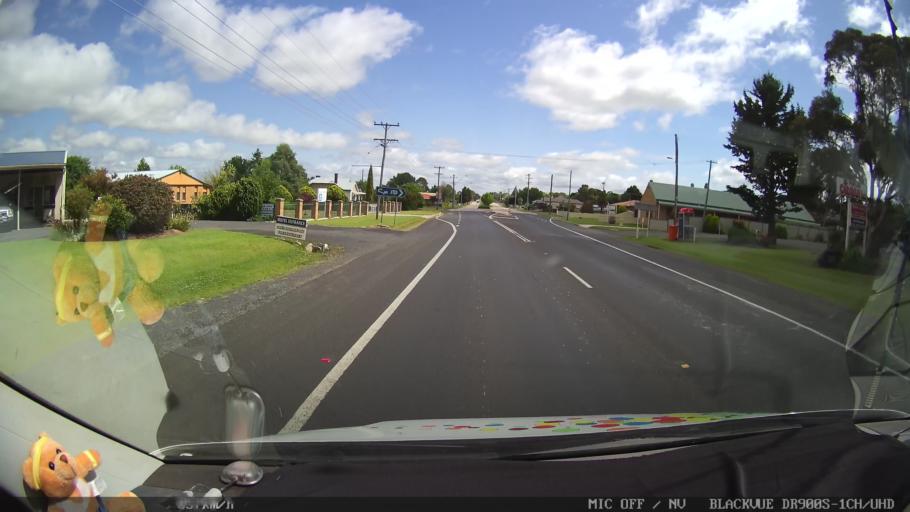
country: AU
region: New South Wales
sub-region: Glen Innes Severn
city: Glen Innes
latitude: -29.7521
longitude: 151.7355
